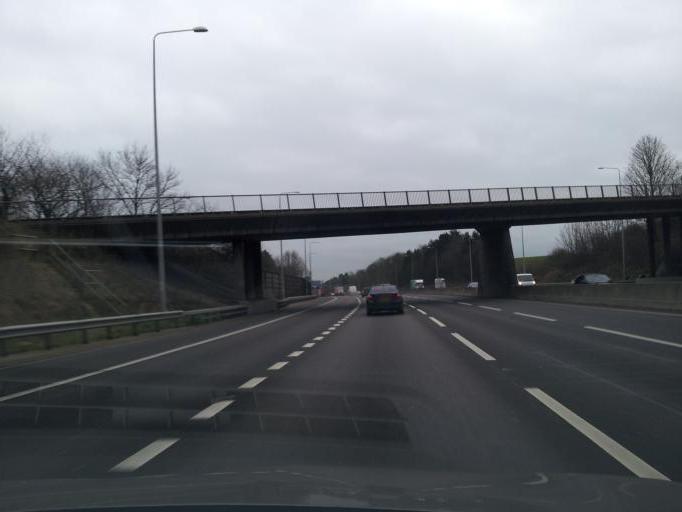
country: GB
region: England
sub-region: Derbyshire
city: Long Eaton
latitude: 52.9285
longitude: -1.3001
